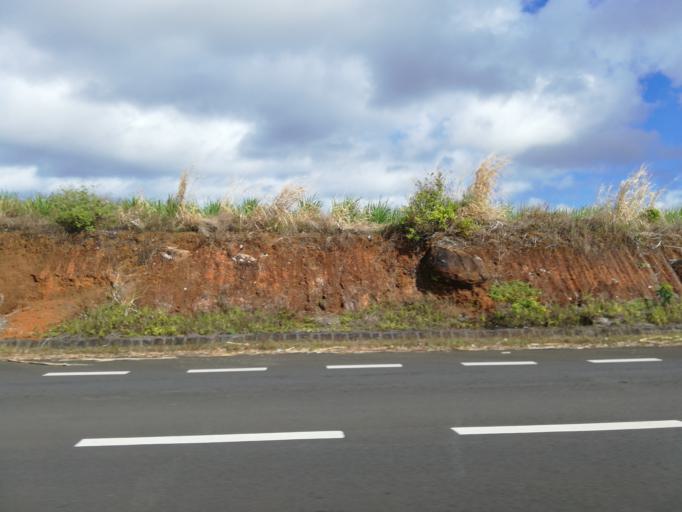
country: MU
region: Grand Port
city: Mahebourg
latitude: -20.4021
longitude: 57.6799
